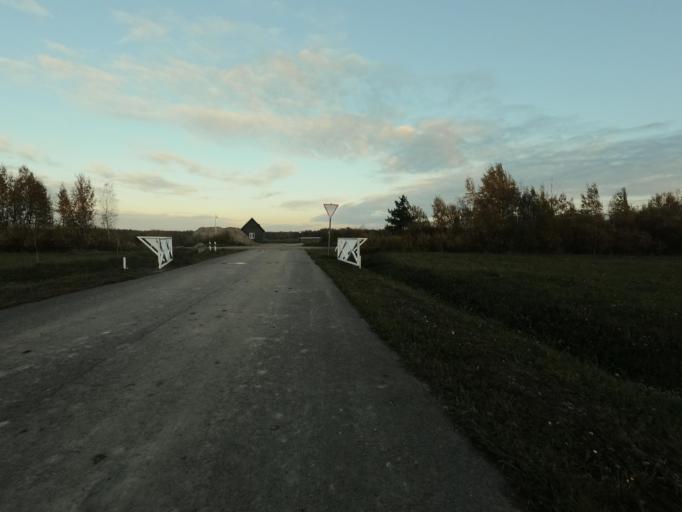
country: RU
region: Leningrad
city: Mga
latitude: 59.7895
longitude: 31.2011
